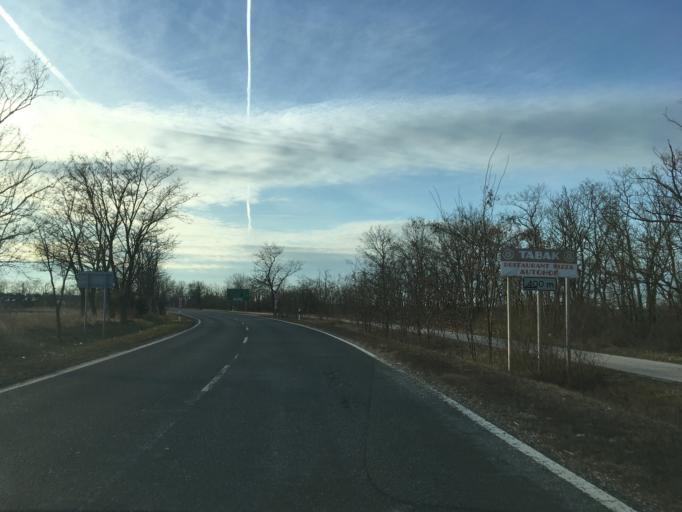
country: AT
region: Burgenland
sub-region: Politischer Bezirk Neusiedl am See
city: Nickelsdorf
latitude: 47.9267
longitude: 17.1243
